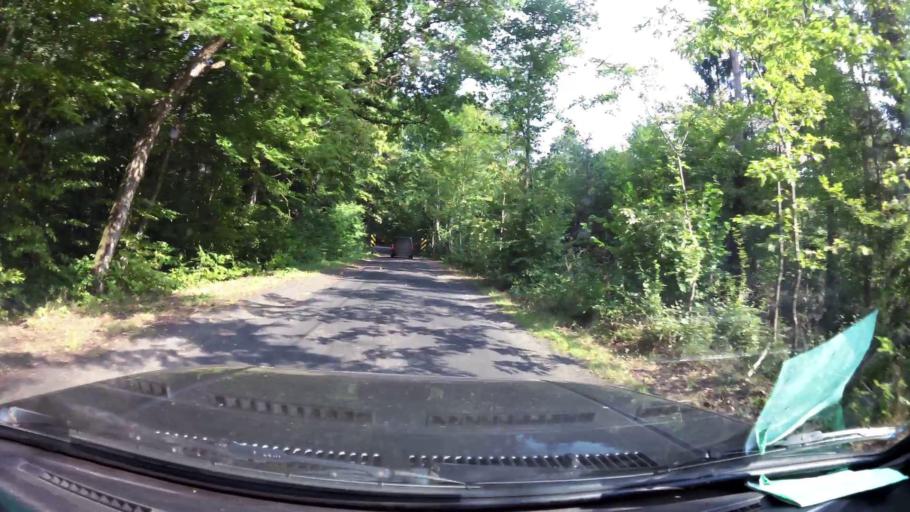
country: PL
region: West Pomeranian Voivodeship
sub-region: Powiat koszalinski
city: Bobolice
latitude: 54.1021
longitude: 16.4965
